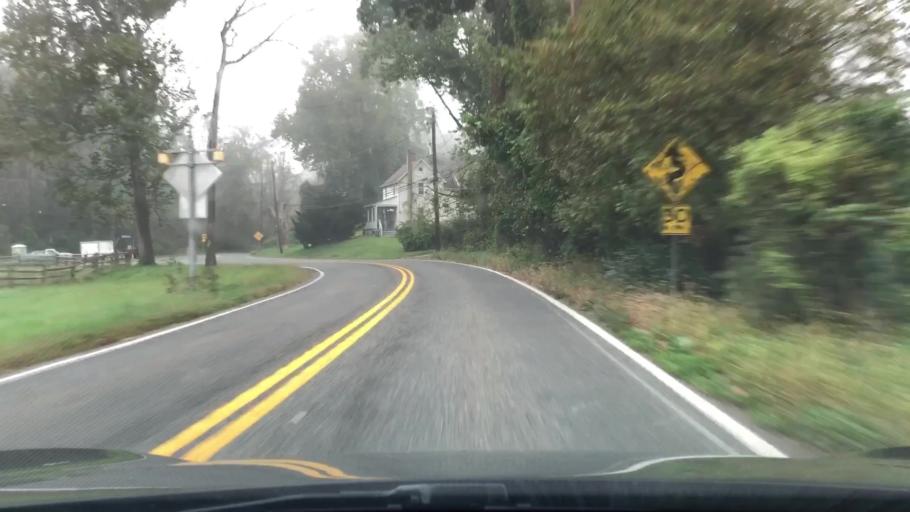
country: US
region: Pennsylvania
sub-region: Delaware County
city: Wayne
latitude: 40.0123
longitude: -75.3860
